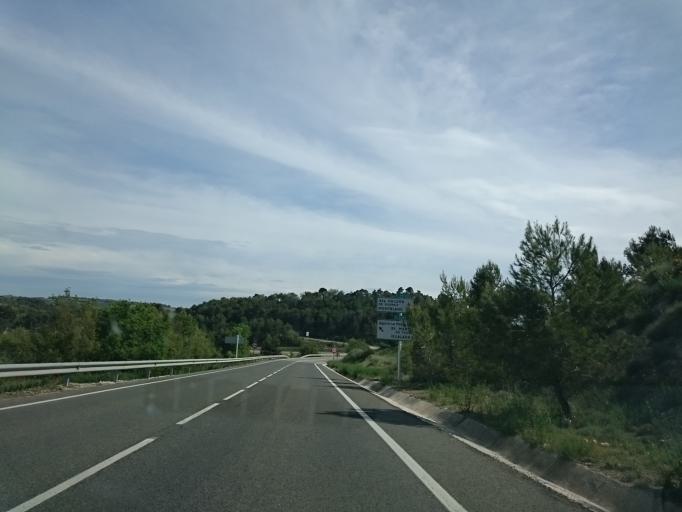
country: ES
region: Catalonia
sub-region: Provincia de Tarragona
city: Santa Coloma de Queralt
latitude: 41.5567
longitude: 1.4047
